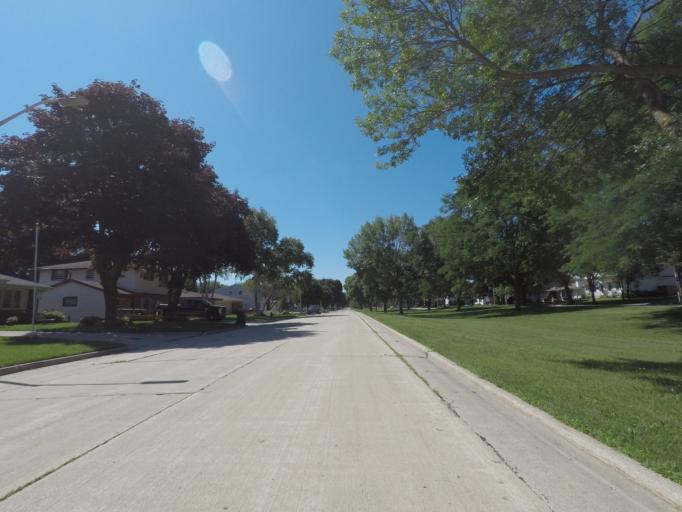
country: US
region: Wisconsin
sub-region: Waukesha County
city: Elm Grove
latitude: 43.0231
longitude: -88.0619
